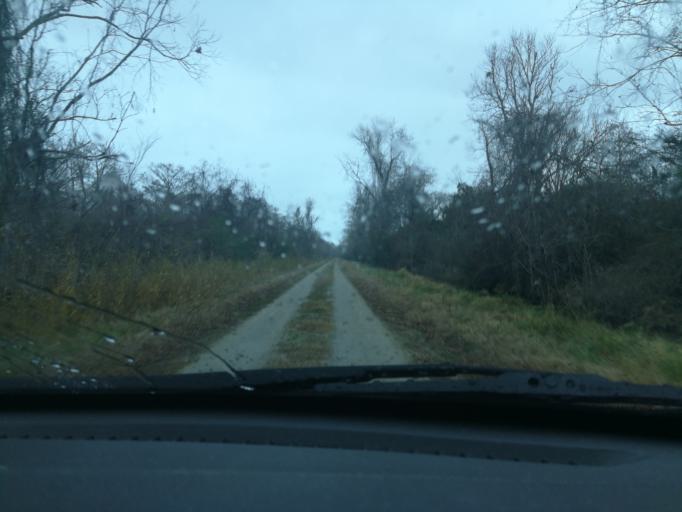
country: US
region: North Carolina
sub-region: Hyde County
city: Swanquarter
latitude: 35.4738
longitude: -76.1333
